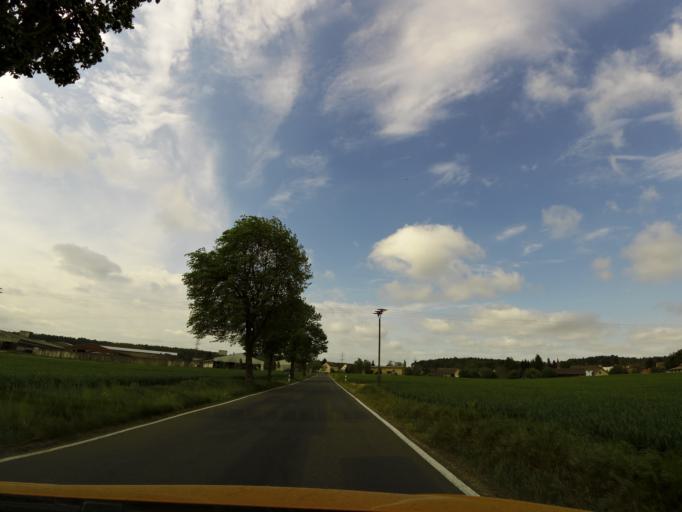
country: DE
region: Brandenburg
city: Belzig
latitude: 52.0990
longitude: 12.6229
